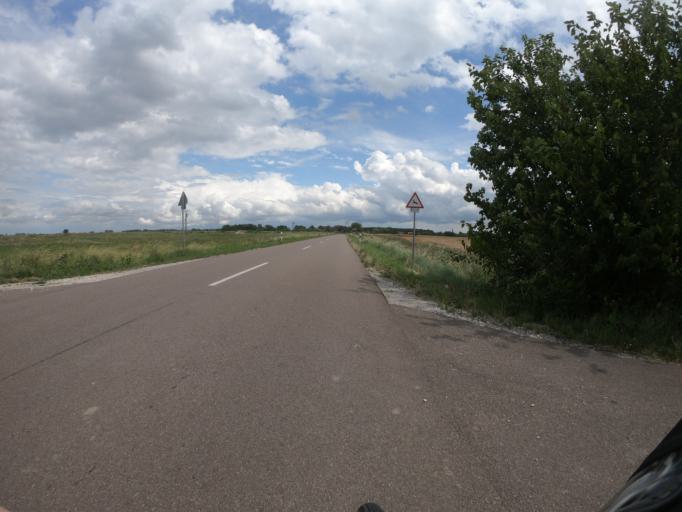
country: HU
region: Jasz-Nagykun-Szolnok
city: Tiszafured
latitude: 47.6909
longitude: 20.7986
